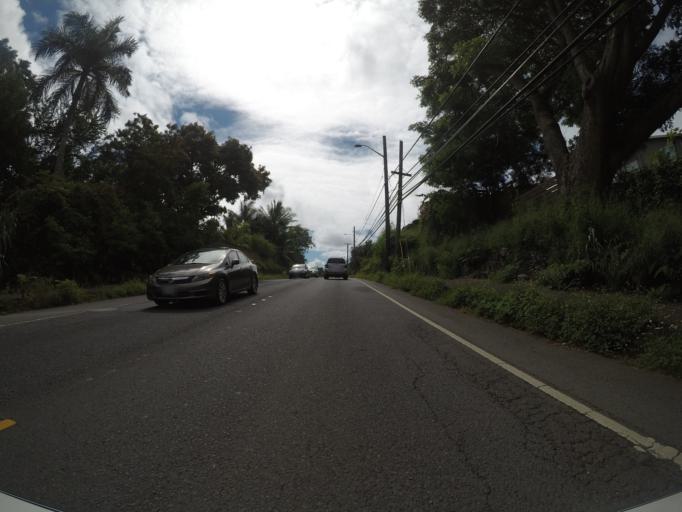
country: US
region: Hawaii
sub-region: Honolulu County
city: Waimanalo
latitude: 21.3477
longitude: -157.7202
